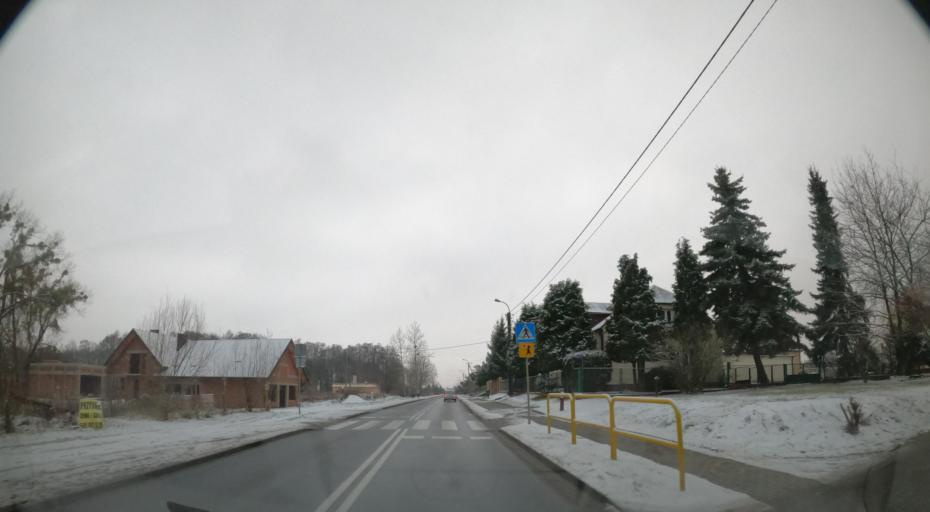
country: PL
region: Kujawsko-Pomorskie
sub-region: Powiat lipnowski
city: Wielgie
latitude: 52.7448
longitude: 19.2600
